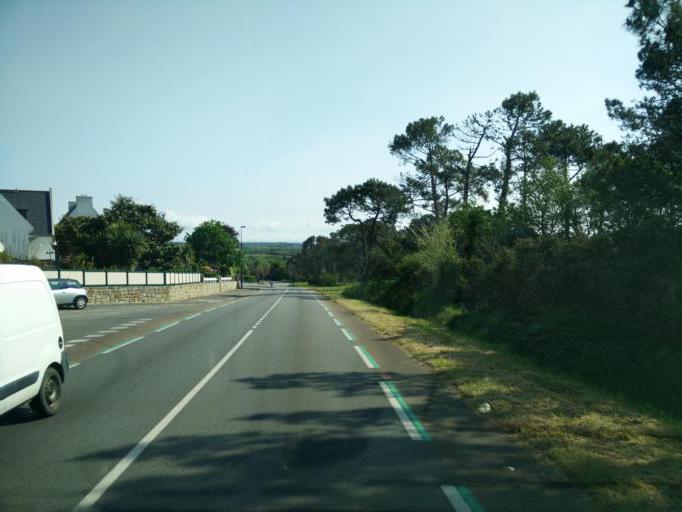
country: FR
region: Brittany
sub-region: Departement du Finistere
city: Crozon
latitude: 48.2440
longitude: -4.4763
